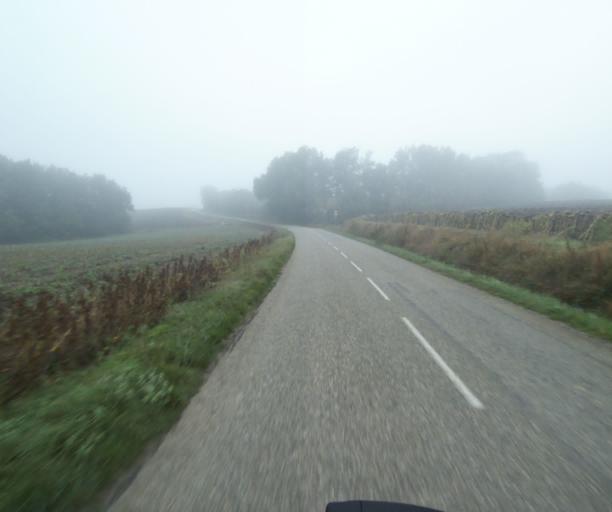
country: FR
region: Midi-Pyrenees
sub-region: Departement du Tarn-et-Garonne
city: Saint-Nauphary
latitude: 43.9365
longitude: 1.4194
